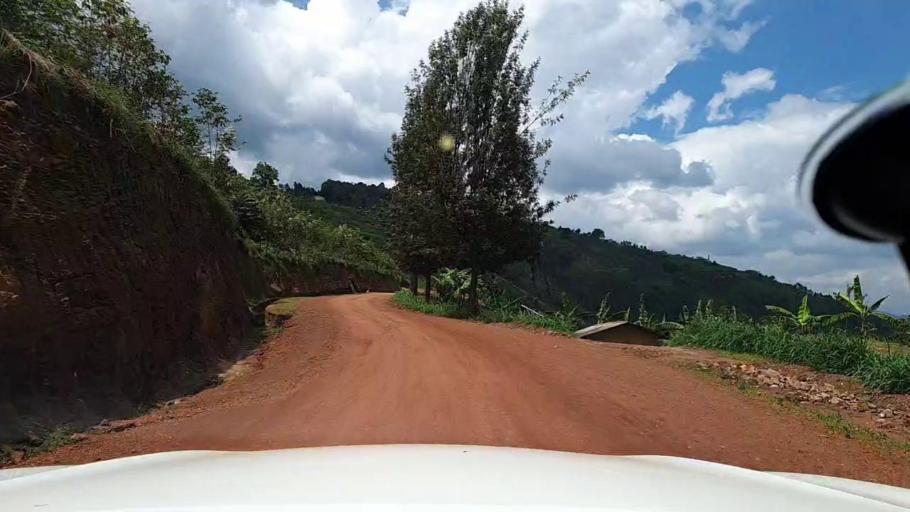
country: RW
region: Northern Province
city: Byumba
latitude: -1.7522
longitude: 29.8452
